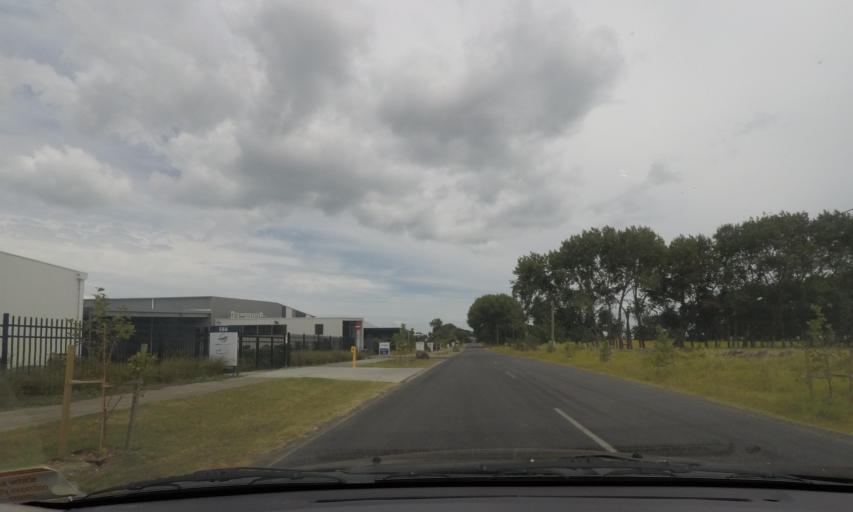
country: NZ
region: Auckland
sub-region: Auckland
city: Mangere
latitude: -36.9893
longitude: 174.7601
